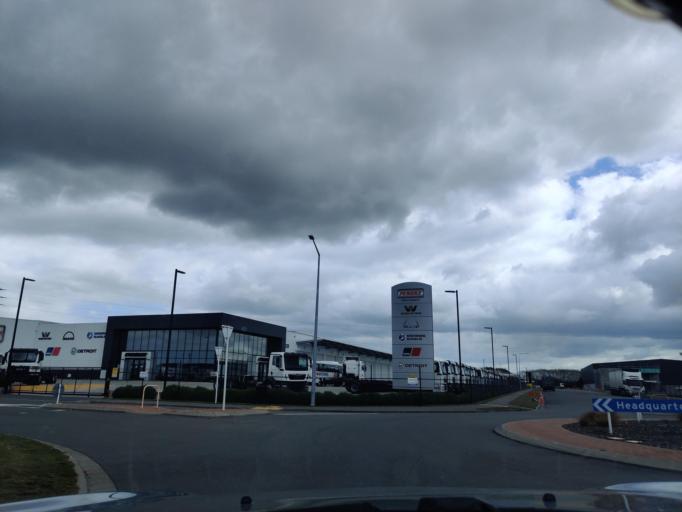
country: NZ
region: Canterbury
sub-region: Selwyn District
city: Prebbleton
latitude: -43.5551
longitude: 172.5107
